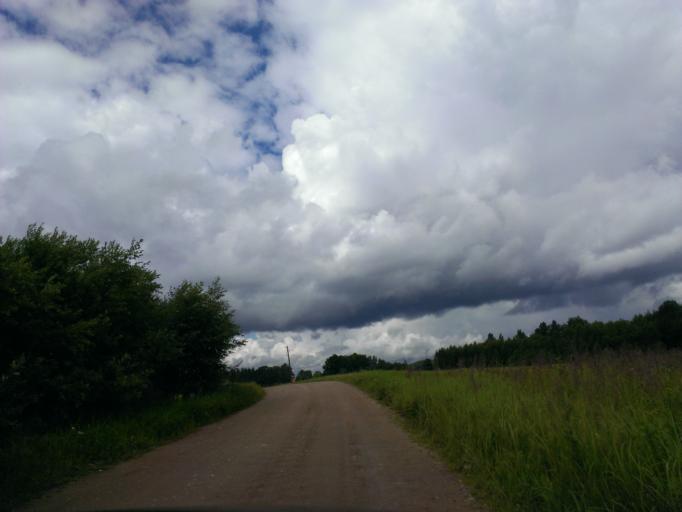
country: LV
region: Ligatne
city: Ligatne
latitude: 57.2182
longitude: 25.0098
